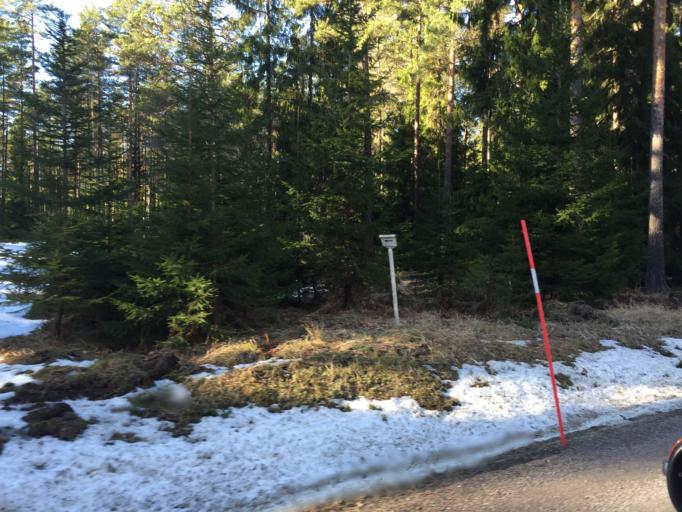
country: SE
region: Soedermanland
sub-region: Vingakers Kommun
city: Vingaker
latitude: 58.9690
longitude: 15.6754
